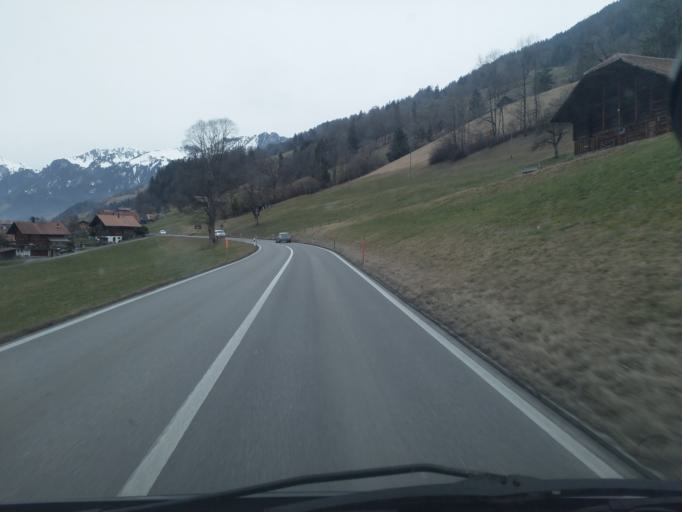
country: CH
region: Bern
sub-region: Frutigen-Niedersimmental District
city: Erlenbach im Simmental
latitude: 46.6584
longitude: 7.5108
